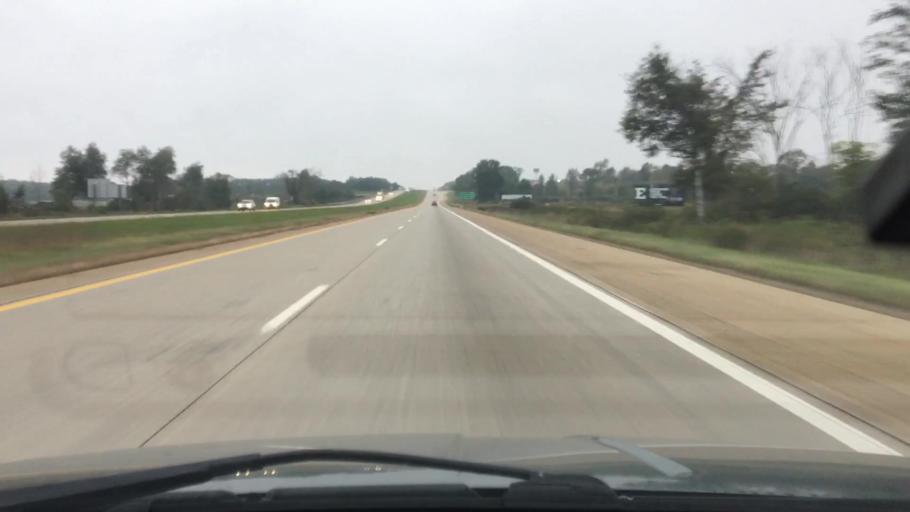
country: US
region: Michigan
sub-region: Jackson County
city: Concord
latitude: 42.2624
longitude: -84.6366
